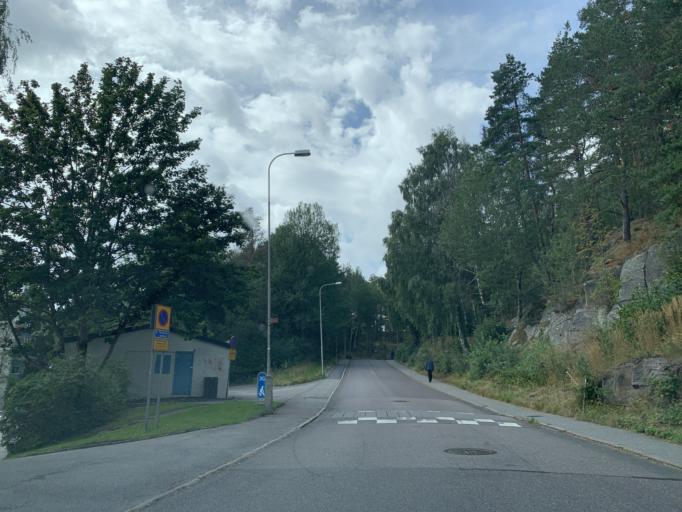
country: SE
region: Vaestra Goetaland
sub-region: Goteborg
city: Eriksbo
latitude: 57.7570
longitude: 12.0409
